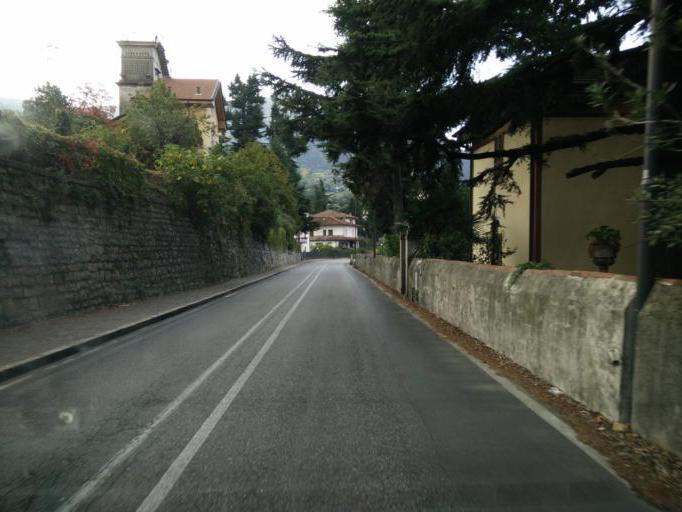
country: IT
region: Lombardy
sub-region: Provincia di Brescia
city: Sulzano
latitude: 45.6937
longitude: 10.1036
